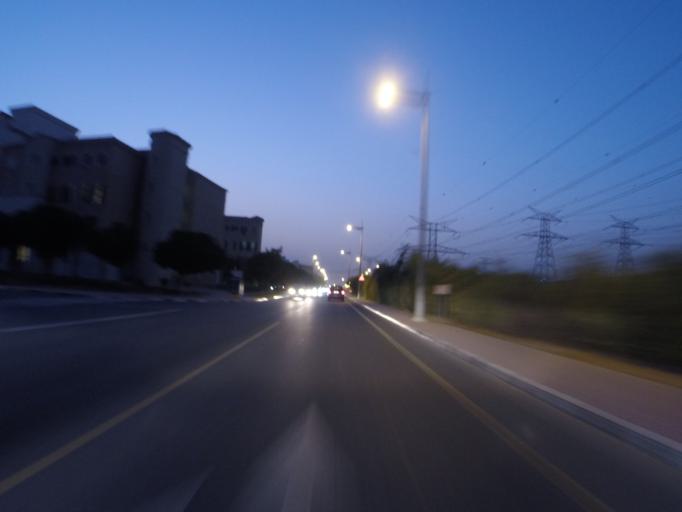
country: AE
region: Dubai
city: Dubai
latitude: 25.0477
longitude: 55.1381
